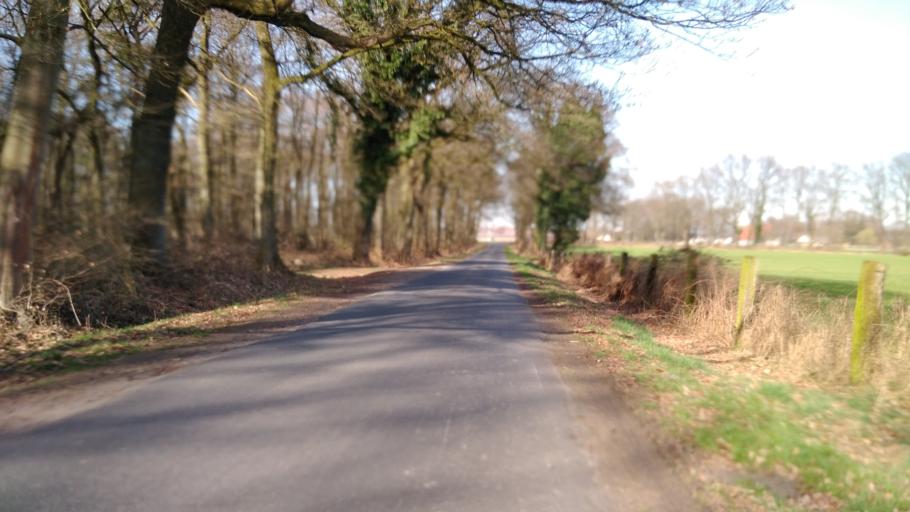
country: DE
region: North Rhine-Westphalia
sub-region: Regierungsbezirk Munster
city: Gladbeck
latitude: 51.5876
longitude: 6.9279
